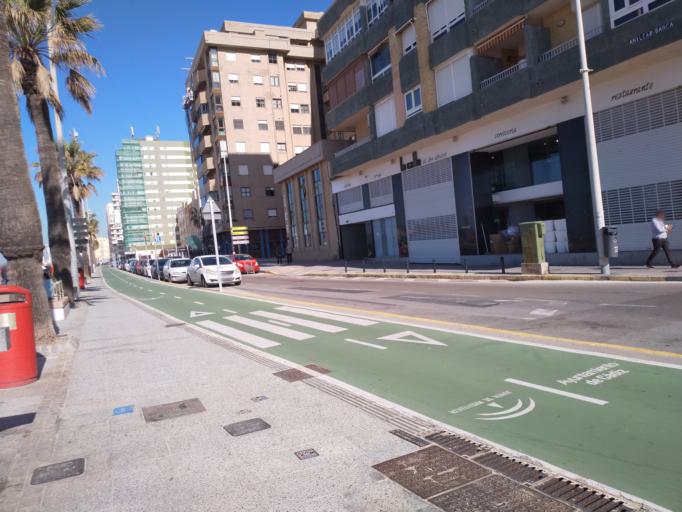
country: ES
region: Andalusia
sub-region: Provincia de Cadiz
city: Cadiz
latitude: 36.5076
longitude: -6.2795
